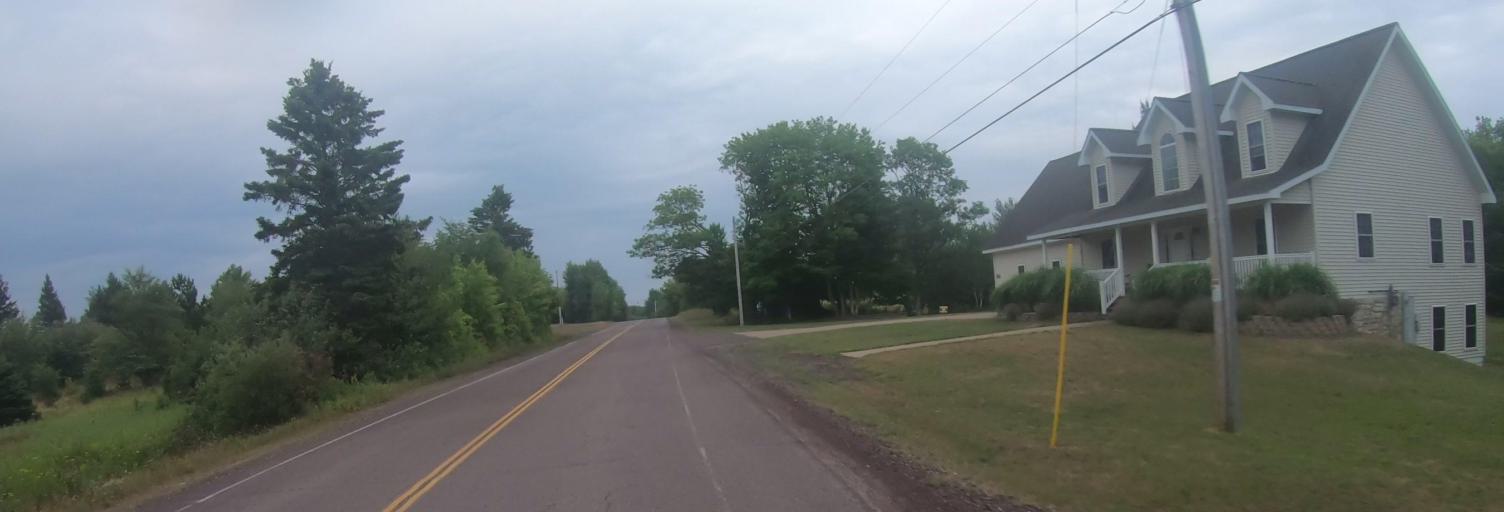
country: US
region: Michigan
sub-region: Houghton County
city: Laurium
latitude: 47.3003
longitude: -88.3566
